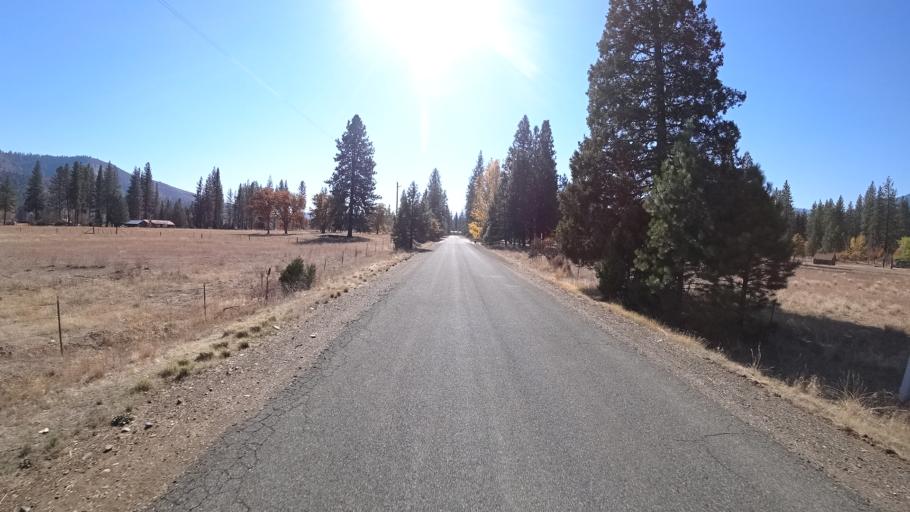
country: US
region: California
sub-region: Siskiyou County
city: Yreka
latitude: 41.6062
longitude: -122.9699
